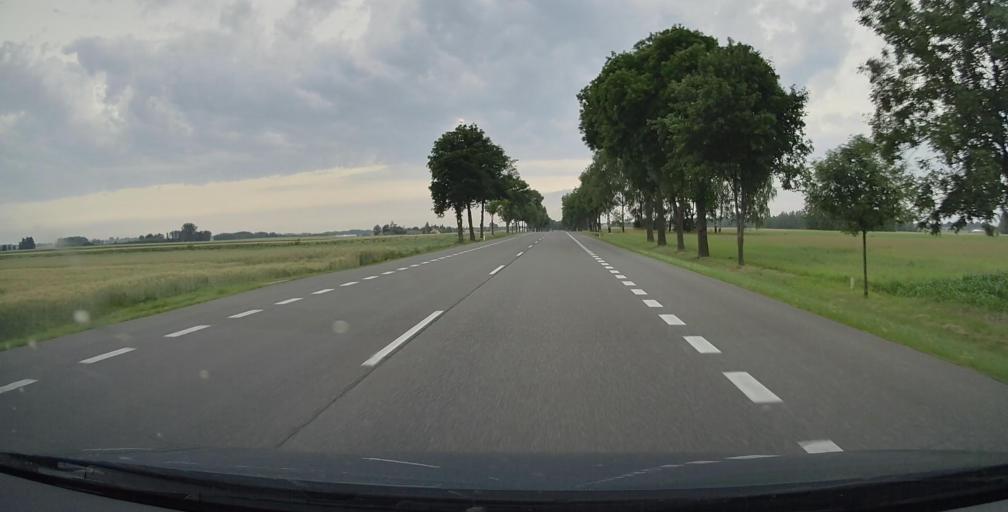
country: PL
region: Lublin Voivodeship
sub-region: Powiat lukowski
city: Trzebieszow
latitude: 52.0591
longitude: 22.5761
